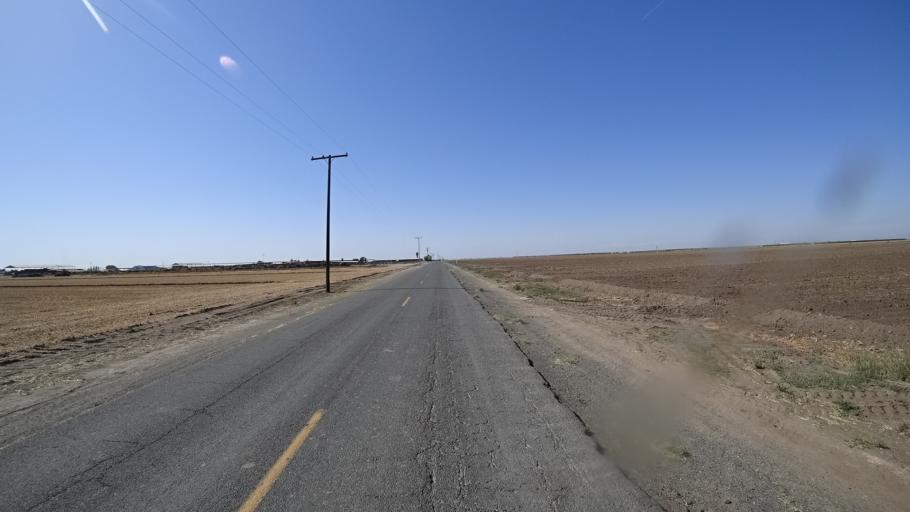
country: US
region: California
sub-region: Kings County
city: Corcoran
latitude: 36.2165
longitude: -119.5471
